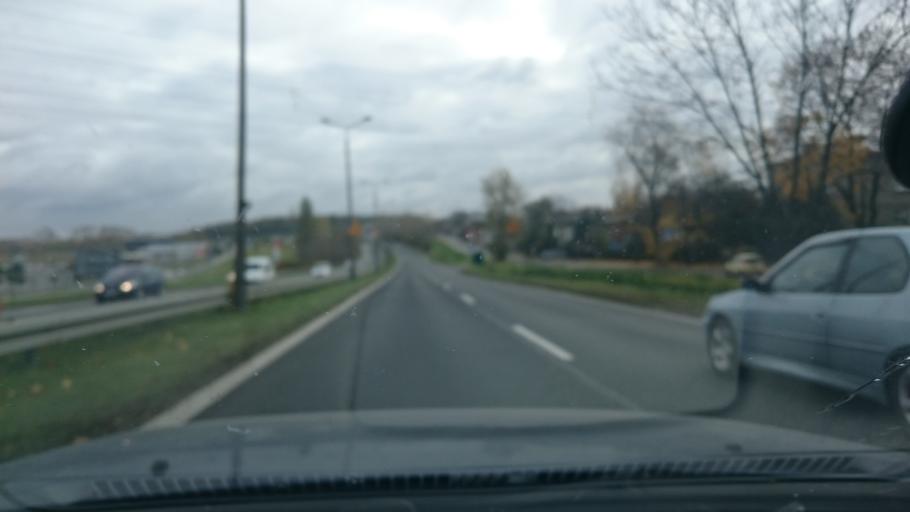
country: PL
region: Silesian Voivodeship
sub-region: Powiat bedzinski
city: Bedzin
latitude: 50.3003
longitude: 19.1592
